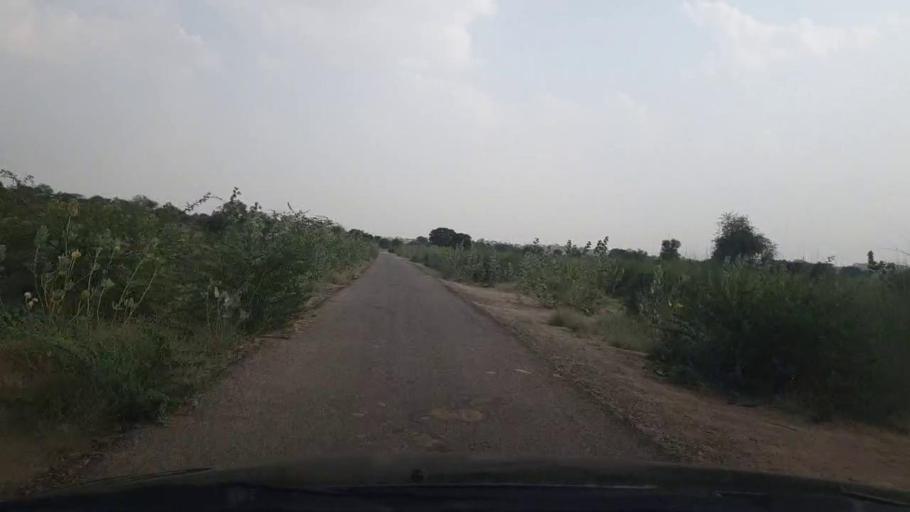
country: PK
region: Sindh
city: Islamkot
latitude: 25.0061
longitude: 70.5981
